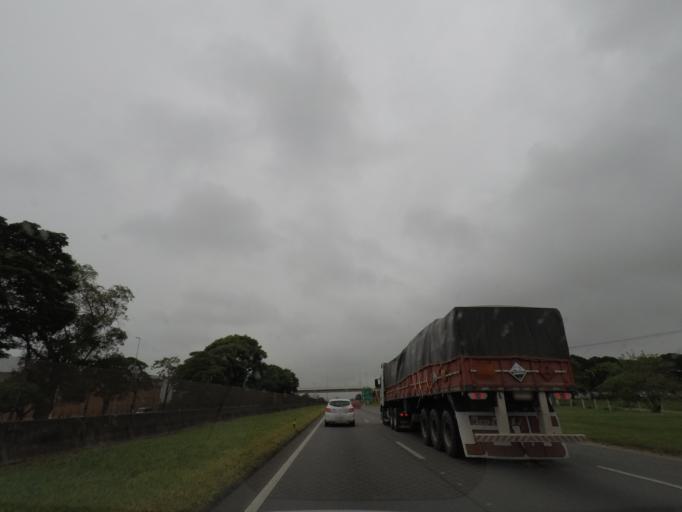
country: BR
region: Sao Paulo
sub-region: Cacapava
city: Cacapava
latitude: -23.1181
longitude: -45.7181
